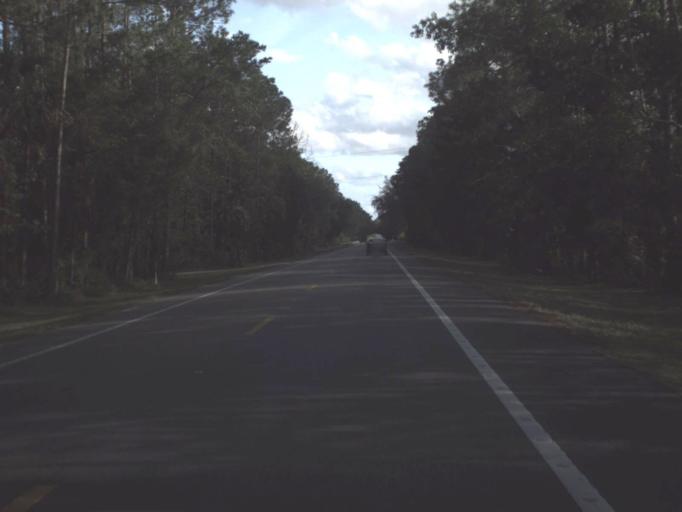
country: US
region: Florida
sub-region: Flagler County
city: Bunnell
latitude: 29.3636
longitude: -81.3116
